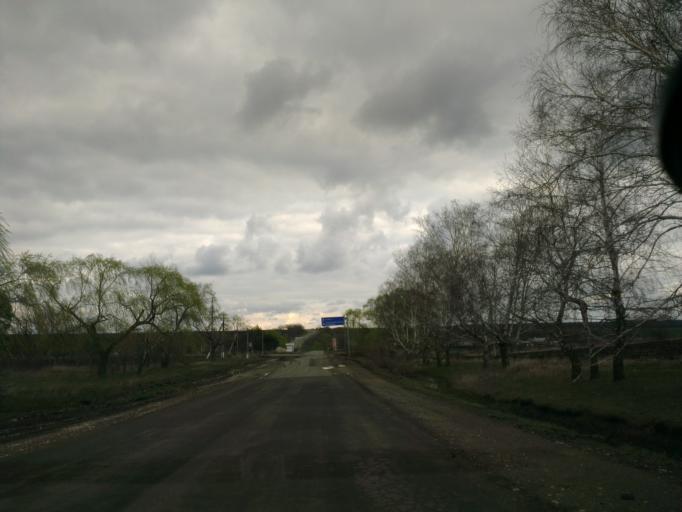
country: MD
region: Gagauzia
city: Comrat
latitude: 46.3111
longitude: 28.5684
